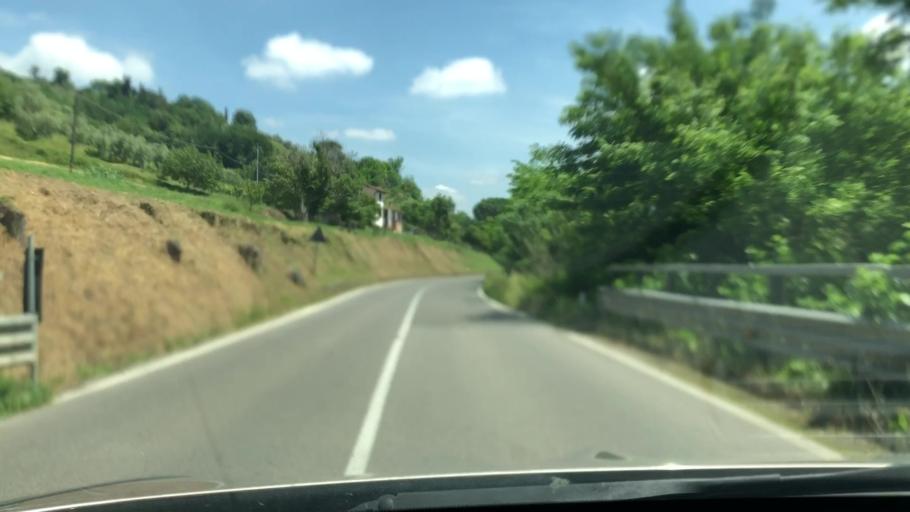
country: IT
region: Tuscany
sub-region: Province of Pisa
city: Forcoli
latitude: 43.6080
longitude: 10.6937
